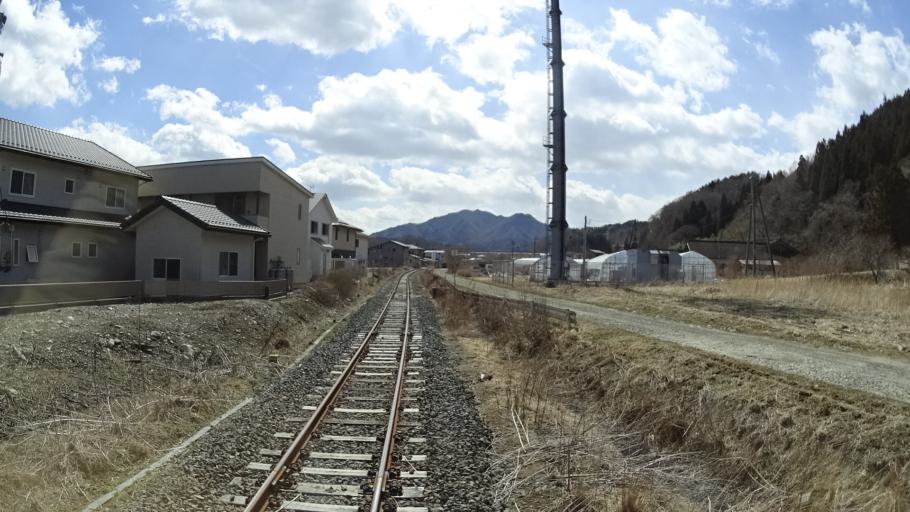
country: JP
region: Iwate
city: Yamada
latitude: 39.5331
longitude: 141.9245
